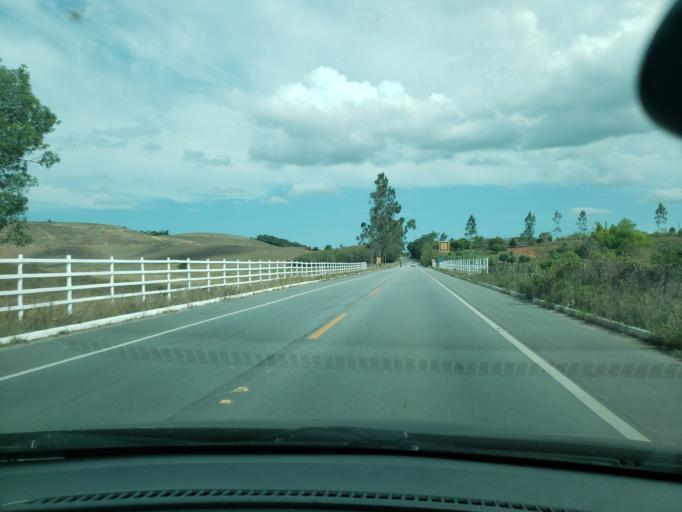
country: BR
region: Alagoas
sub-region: Murici
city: Murici
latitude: -9.3229
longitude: -35.9249
